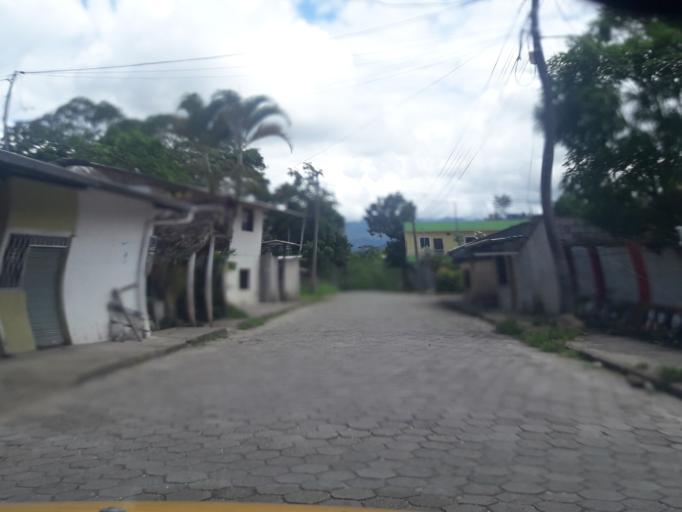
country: EC
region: Napo
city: Tena
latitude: -1.0070
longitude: -77.8203
